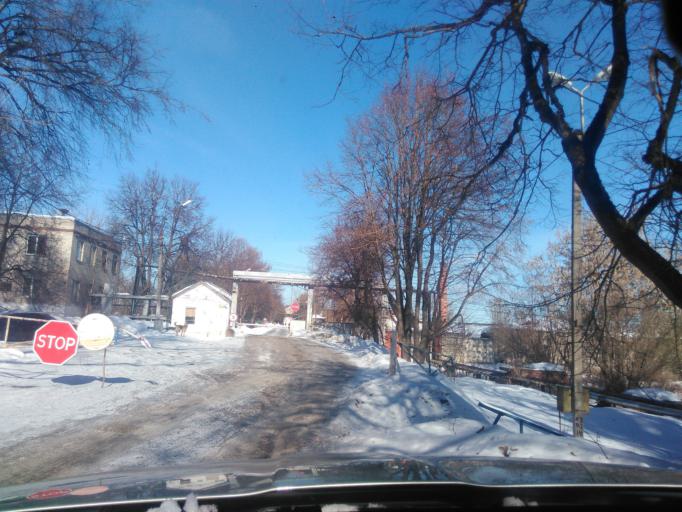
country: RU
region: Moskovskaya
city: Radumlya
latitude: 56.0928
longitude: 37.1516
